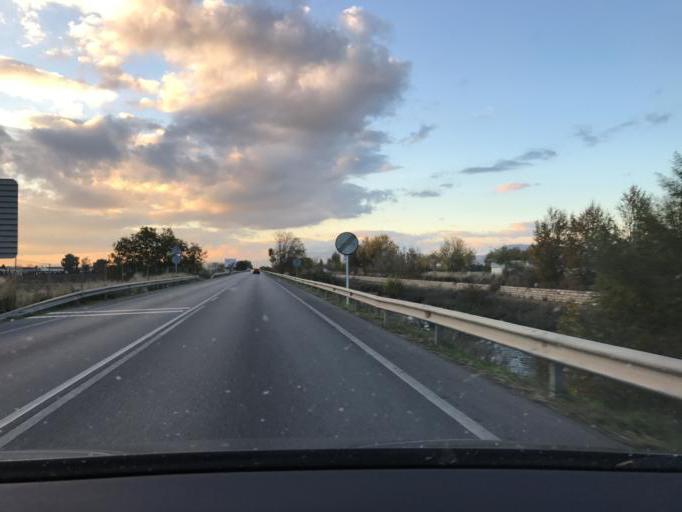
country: ES
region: Andalusia
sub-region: Provincia de Granada
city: Churriana de la Vega
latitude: 37.1638
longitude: -3.6297
